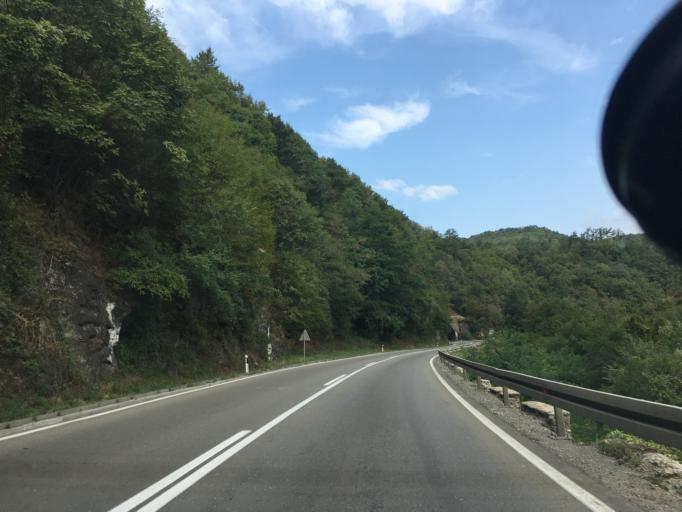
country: RS
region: Central Serbia
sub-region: Moravicki Okrug
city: Lucani
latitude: 43.9087
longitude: 20.2120
